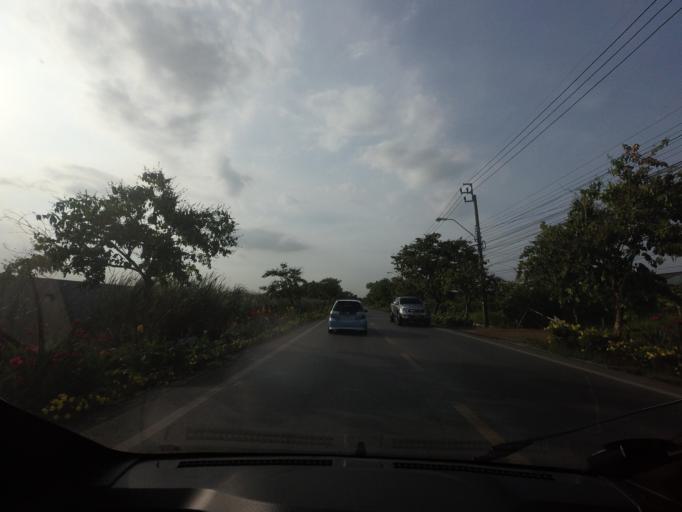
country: TH
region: Bangkok
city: Nong Chok
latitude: 13.8126
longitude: 100.8714
